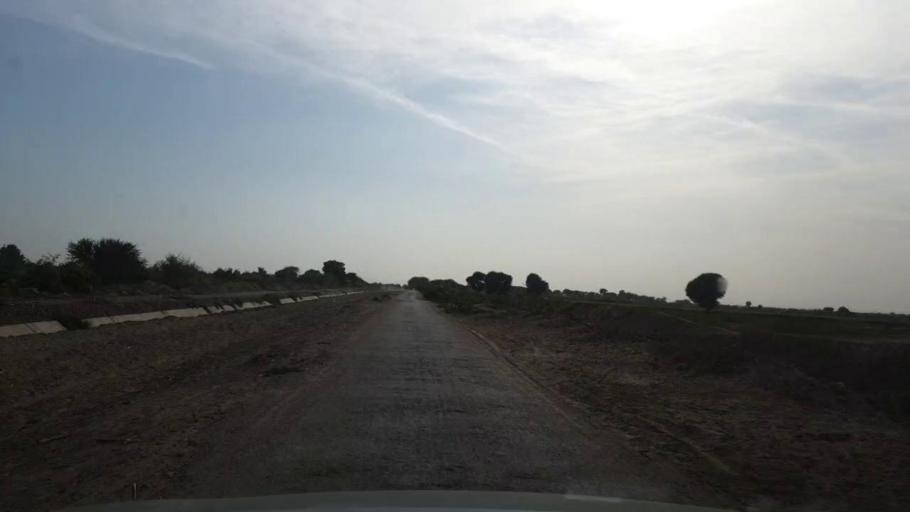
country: PK
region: Sindh
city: Kunri
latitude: 25.1547
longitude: 69.5110
